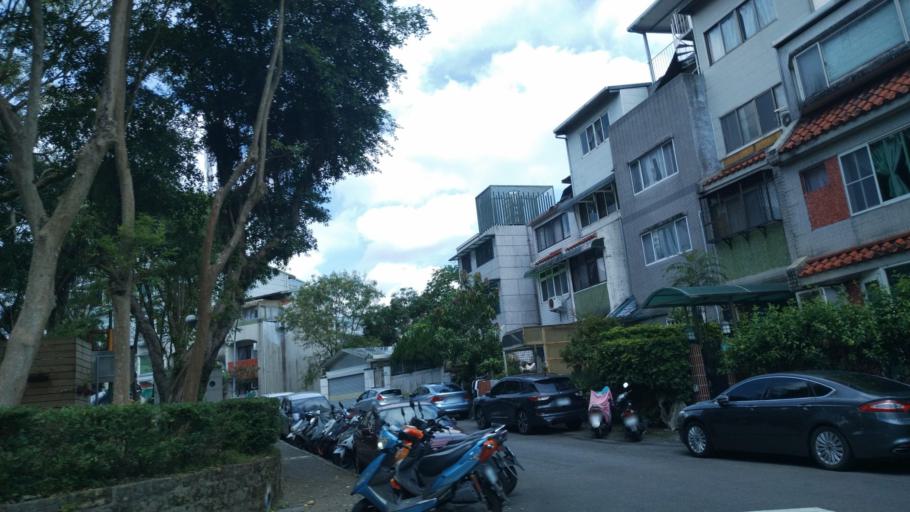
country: TW
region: Taipei
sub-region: Taipei
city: Banqiao
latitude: 24.9516
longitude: 121.4995
